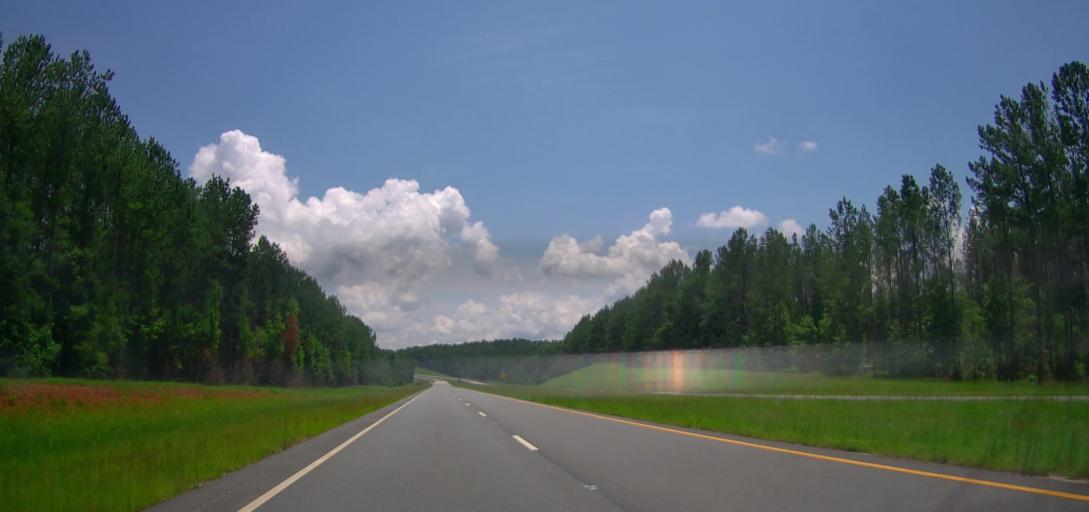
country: US
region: Georgia
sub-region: Upson County
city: Thomaston
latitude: 32.7969
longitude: -84.2695
